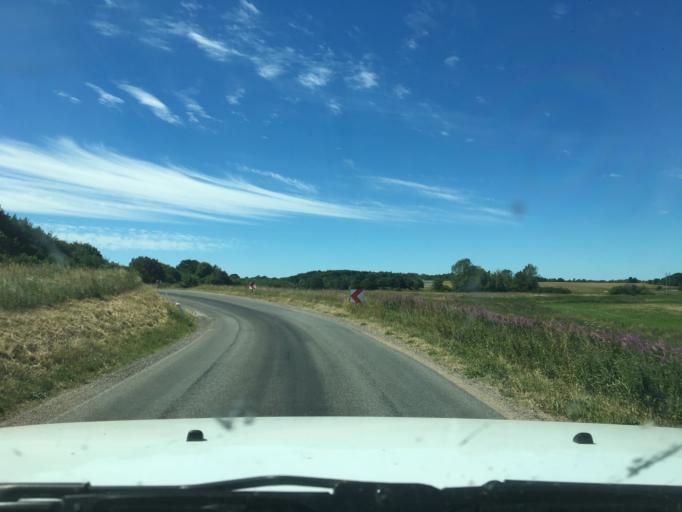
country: DK
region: Central Jutland
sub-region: Syddjurs Kommune
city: Ronde
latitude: 56.3388
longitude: 10.4269
